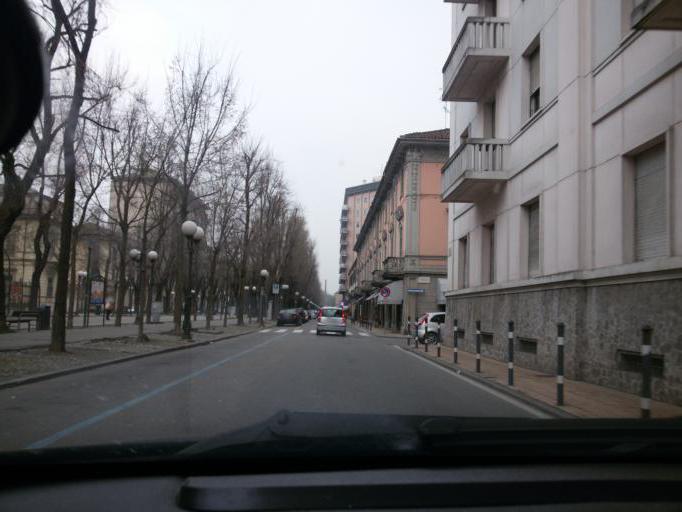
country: IT
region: Piedmont
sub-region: Provincia di Vercelli
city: Vercelli
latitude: 45.3250
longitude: 8.4182
